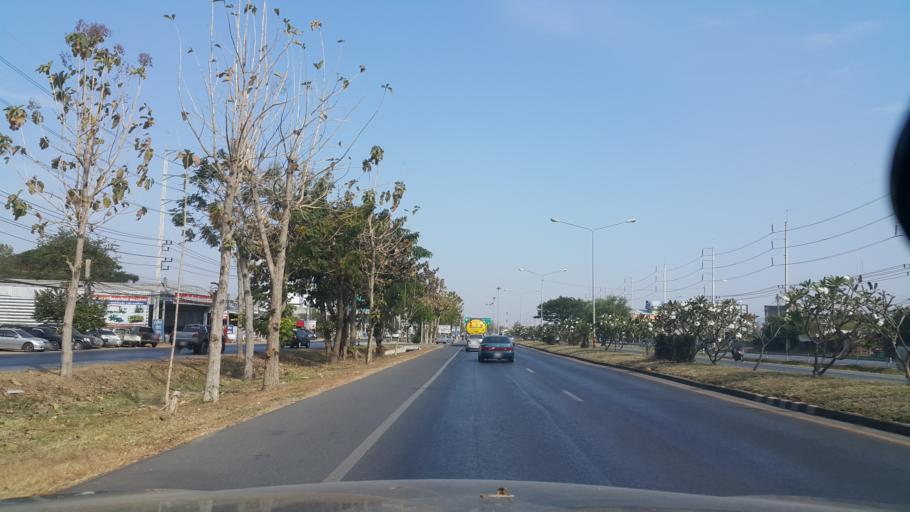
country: TH
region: Nakhon Ratchasima
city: Nakhon Ratchasima
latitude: 14.9529
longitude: 102.0537
